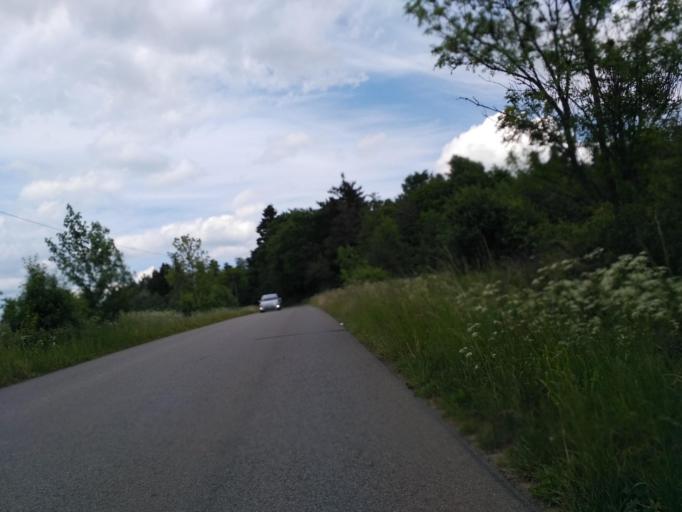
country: PL
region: Subcarpathian Voivodeship
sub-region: Powiat krosnienski
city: Chorkowka
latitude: 49.6219
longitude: 21.6508
